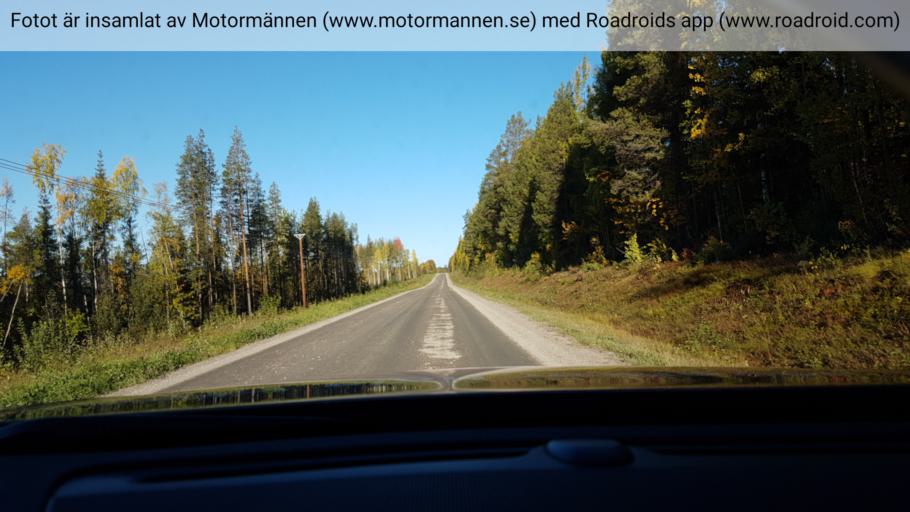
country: SE
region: Norrbotten
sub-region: Alvsbyns Kommun
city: AElvsbyn
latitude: 66.1830
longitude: 21.2177
